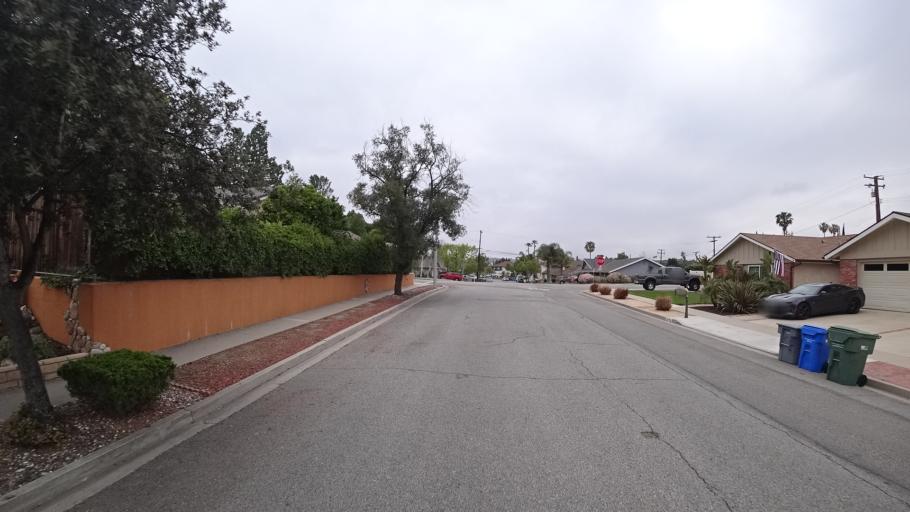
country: US
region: California
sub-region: Ventura County
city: Thousand Oaks
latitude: 34.2081
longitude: -118.8799
